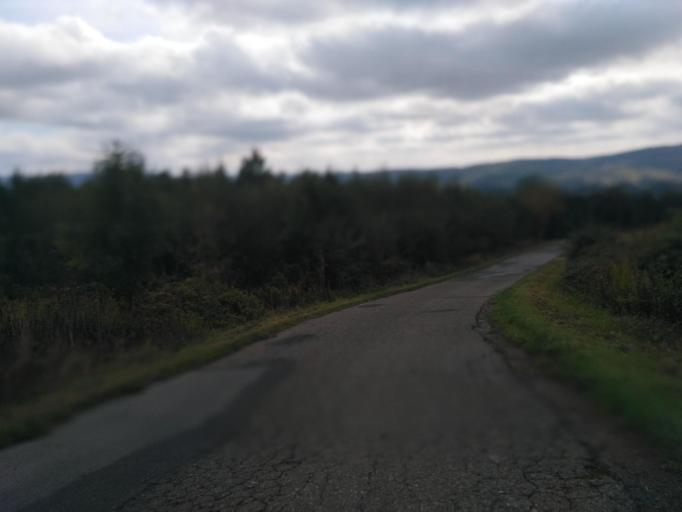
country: PL
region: Subcarpathian Voivodeship
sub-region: Powiat ropczycko-sedziszowski
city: Niedzwiada
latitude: 49.9443
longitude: 21.4619
